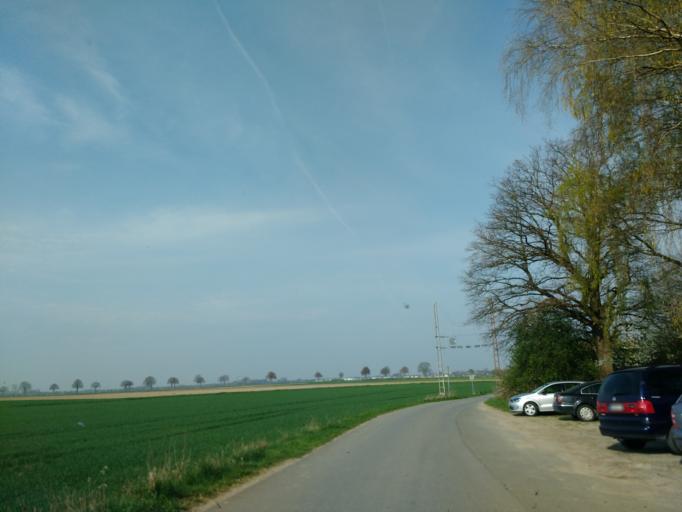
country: DE
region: North Rhine-Westphalia
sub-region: Regierungsbezirk Detmold
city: Salzkotten
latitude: 51.6992
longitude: 8.6333
